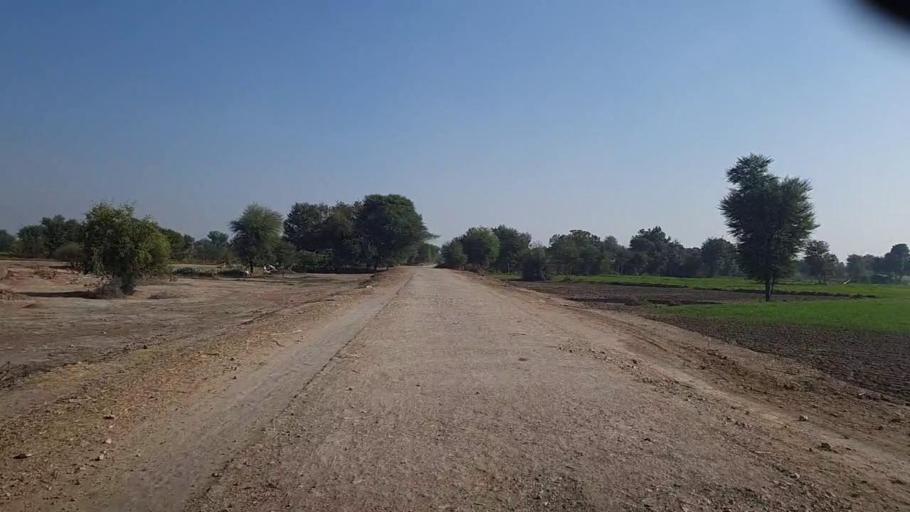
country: PK
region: Sindh
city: Darya Khan Marri
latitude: 26.6644
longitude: 68.3383
